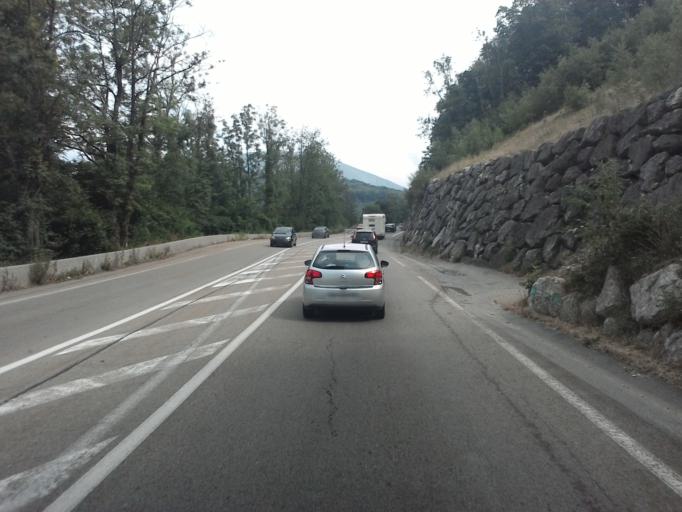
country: FR
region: Rhone-Alpes
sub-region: Departement de l'Isere
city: Notre-Dame-de-Mesage
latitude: 45.0415
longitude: 5.7635
